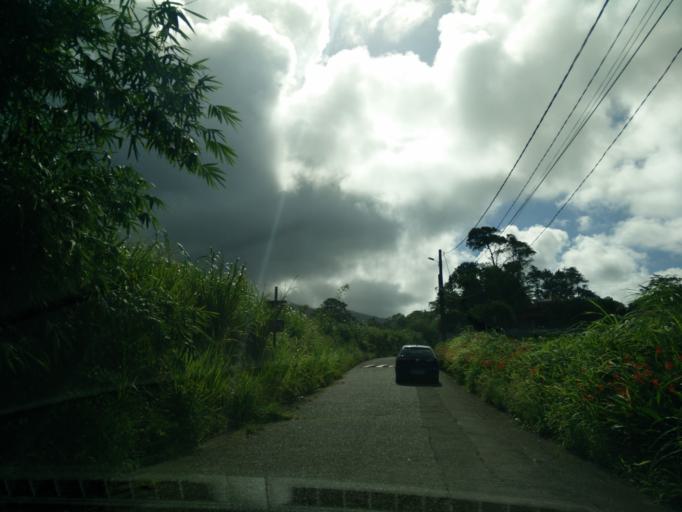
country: MQ
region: Martinique
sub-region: Martinique
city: Basse-Pointe
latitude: 14.8196
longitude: -61.1234
